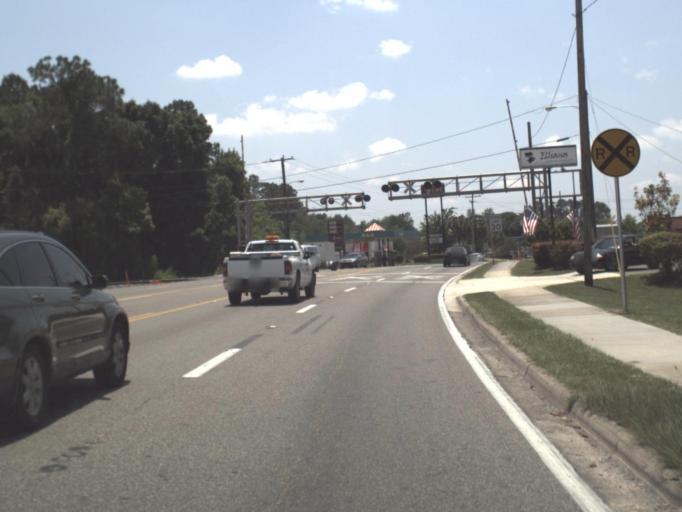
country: US
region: Florida
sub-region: Bradford County
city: Starke
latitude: 29.9410
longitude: -82.1113
